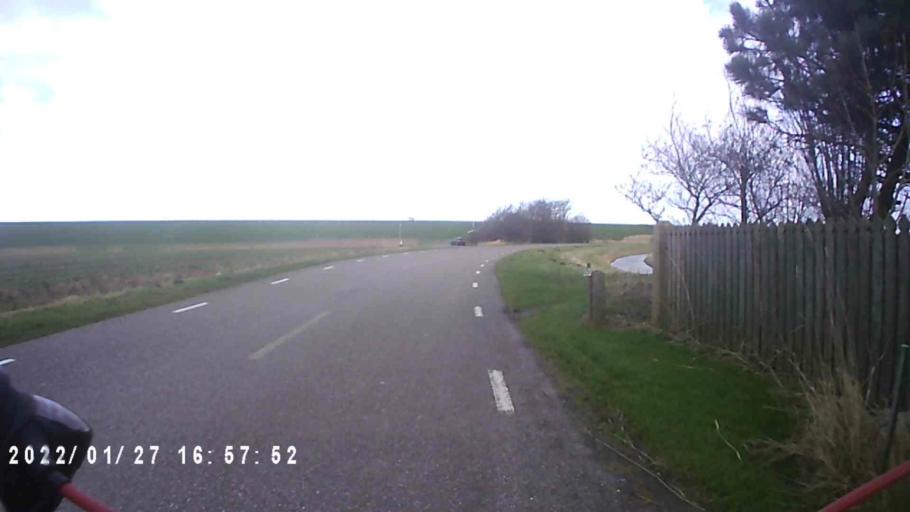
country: NL
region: Friesland
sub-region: Gemeente Dongeradeel
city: Anjum
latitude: 53.4056
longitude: 6.0682
